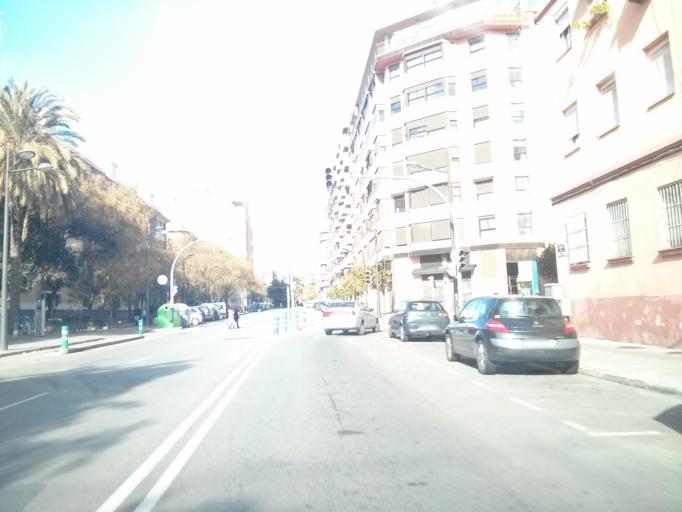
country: ES
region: Valencia
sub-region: Provincia de Valencia
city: Valencia
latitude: 39.4830
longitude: -0.3849
